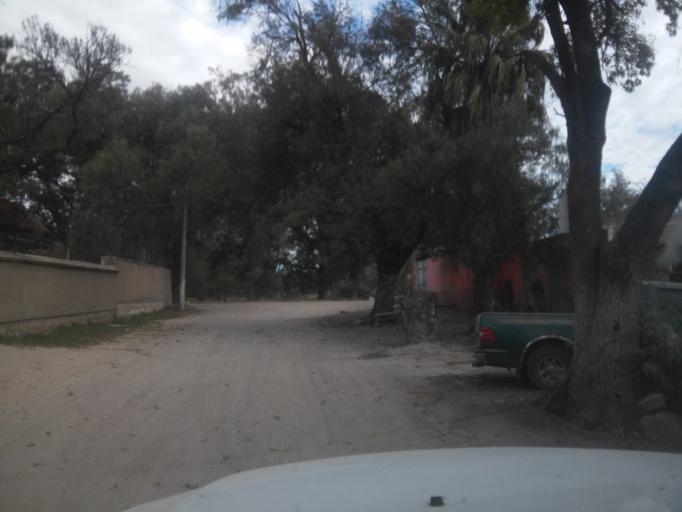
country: MX
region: Durango
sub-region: Durango
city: Jose Refugio Salcido
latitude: 24.0482
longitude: -104.5490
